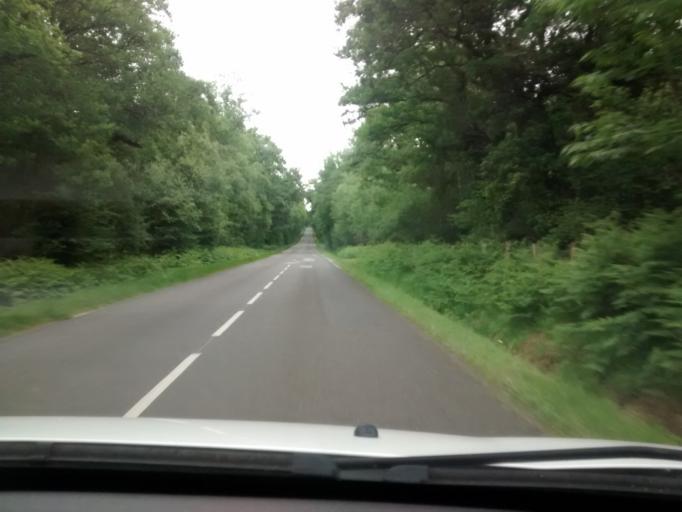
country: FR
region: Brittany
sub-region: Departement d'Ille-et-Vilaine
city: Servon-sur-Vilaine
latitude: 48.1469
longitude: -1.4462
